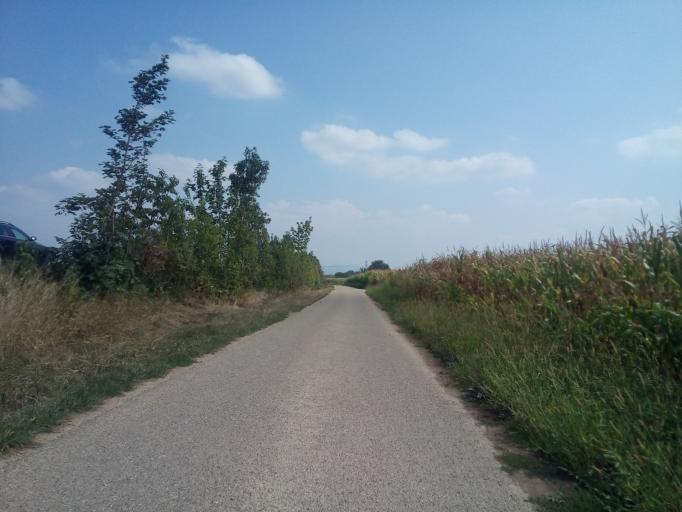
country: DE
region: Baden-Wuerttemberg
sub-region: Freiburg Region
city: Rheinau
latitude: 48.6349
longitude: 7.9088
